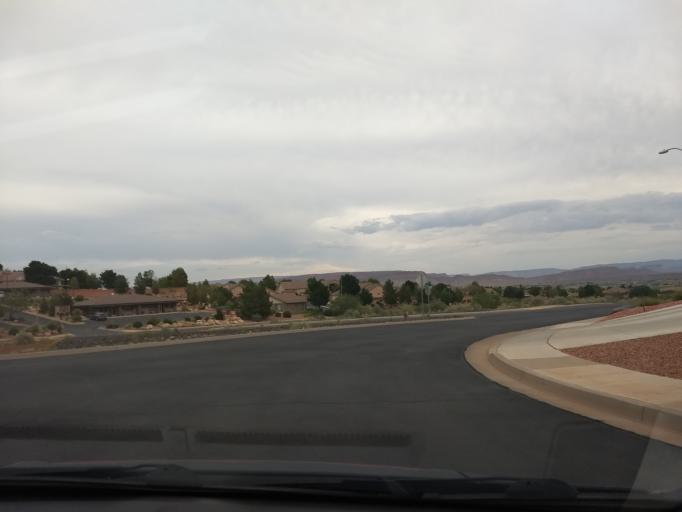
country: US
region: Utah
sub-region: Washington County
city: Saint George
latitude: 37.1113
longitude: -113.5481
